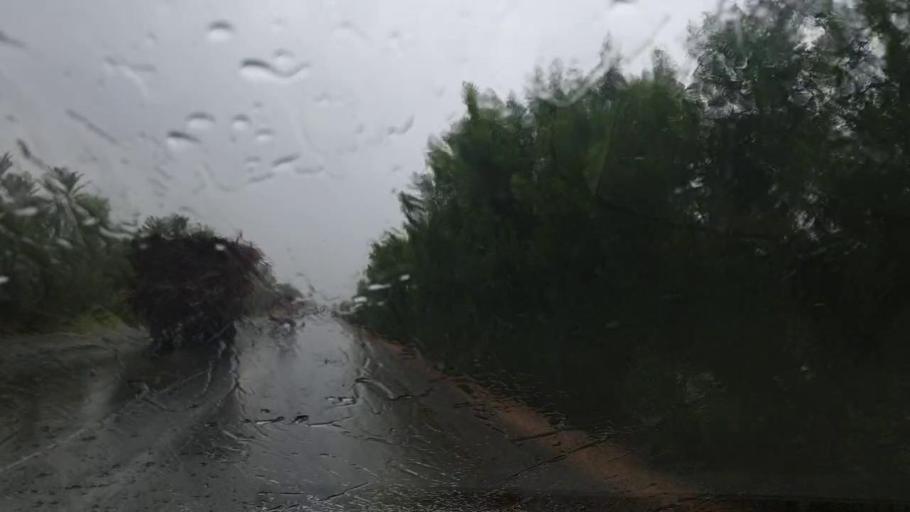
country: PK
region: Sindh
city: Khairpur
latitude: 27.5525
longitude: 68.7338
